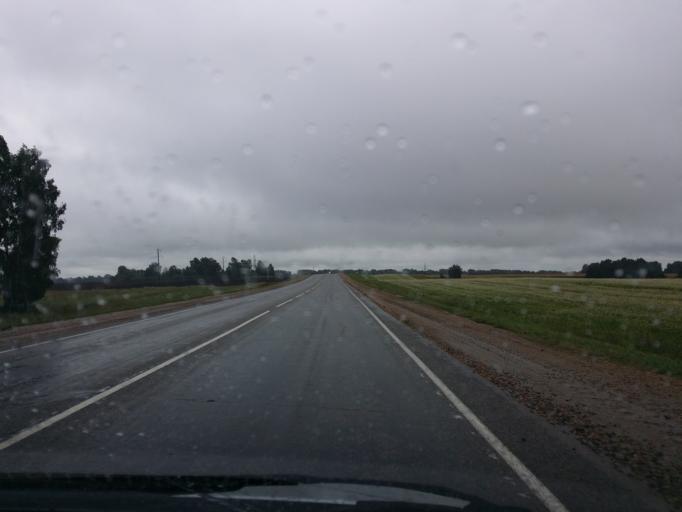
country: RU
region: Altai Krai
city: Nalobikha
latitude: 53.2472
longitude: 84.5765
